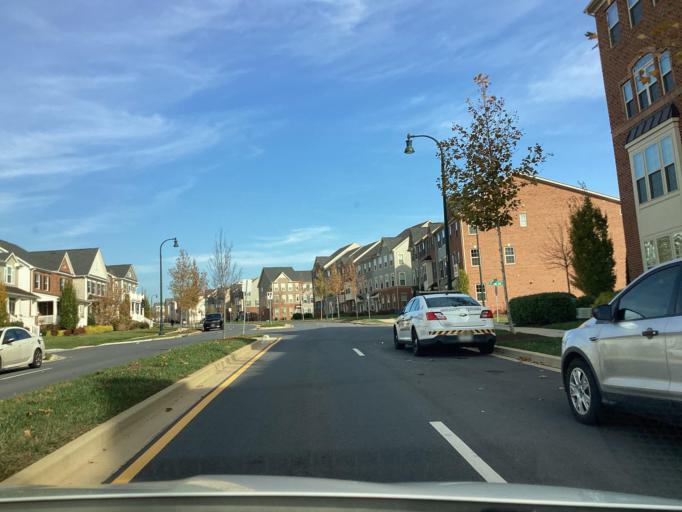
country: US
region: Maryland
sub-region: Montgomery County
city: Clarksburg
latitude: 39.2175
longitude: -77.2854
